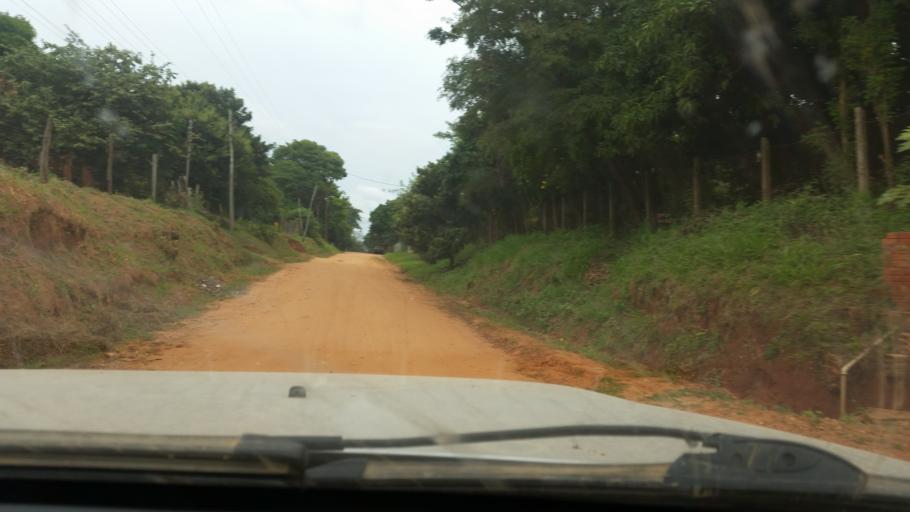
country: PY
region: Guaira
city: Independencia
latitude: -25.7077
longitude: -56.1903
